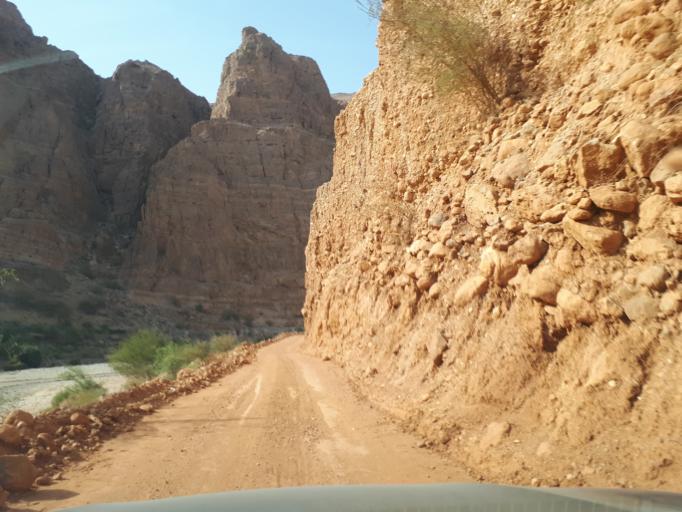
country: OM
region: Ash Sharqiyah
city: Al Qabil
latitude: 23.0683
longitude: 58.9866
